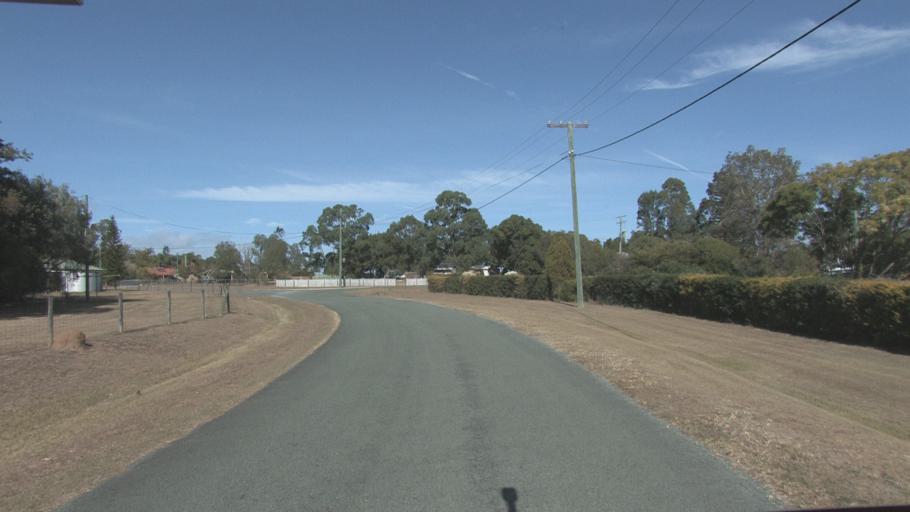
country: AU
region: Queensland
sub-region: Logan
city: Cedar Vale
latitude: -27.8695
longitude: 152.9686
